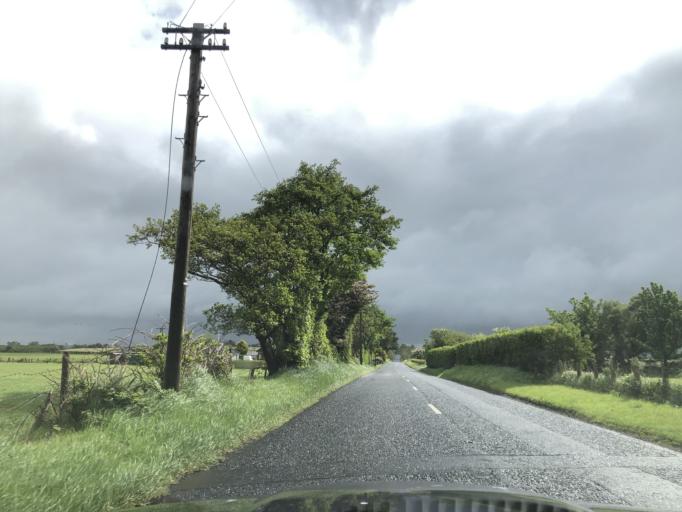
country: GB
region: Northern Ireland
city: Bushmills
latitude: 55.1593
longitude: -6.3904
